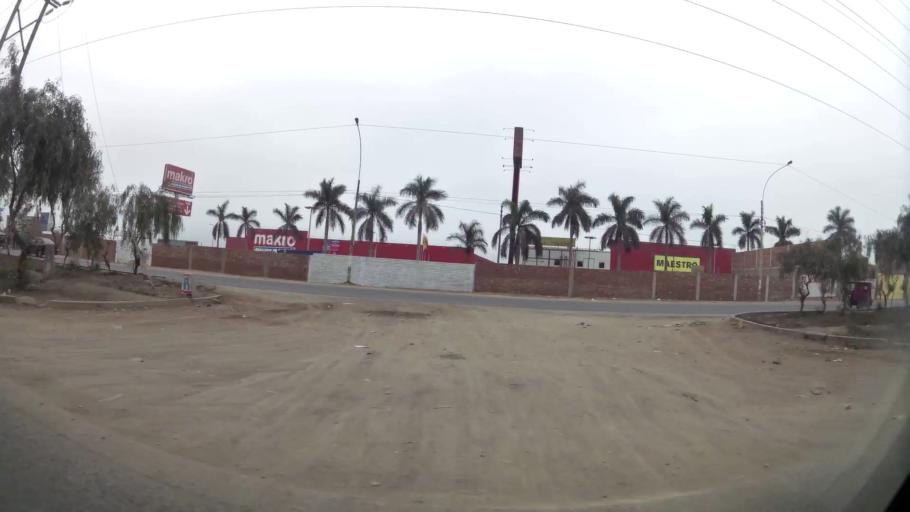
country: PE
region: Lima
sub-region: Lima
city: Urb. Santo Domingo
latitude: -11.9102
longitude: -77.0559
